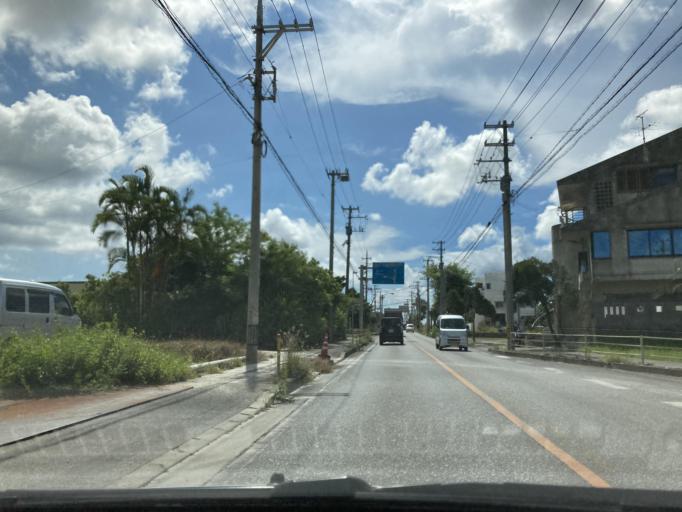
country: JP
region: Okinawa
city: Tomigusuku
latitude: 26.1488
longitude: 127.7244
